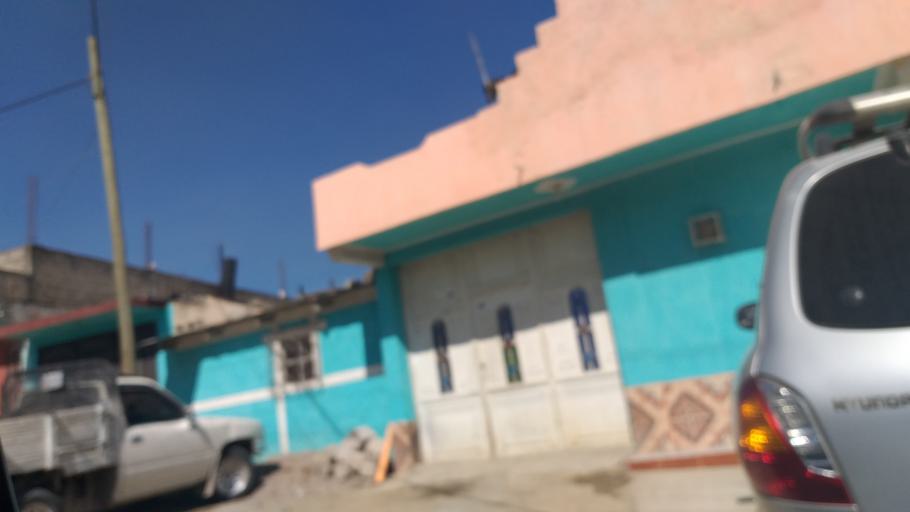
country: GT
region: Quetzaltenango
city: Quetzaltenango
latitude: 14.7993
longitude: -91.5451
